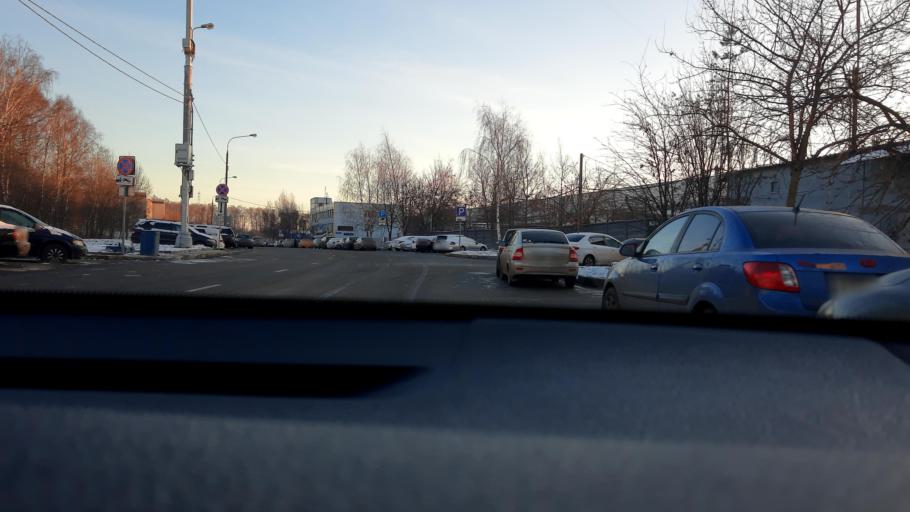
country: RU
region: Moskovskaya
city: Razvilka
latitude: 55.6010
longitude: 37.7366
